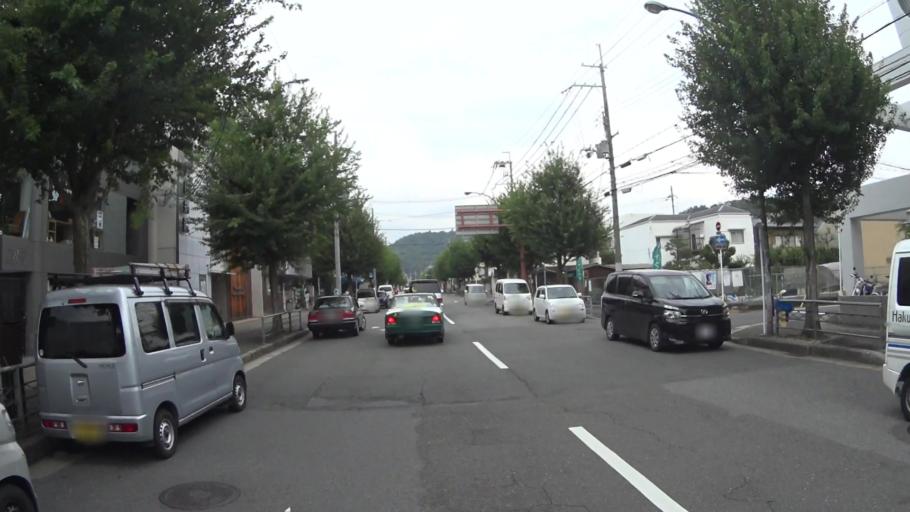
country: JP
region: Kyoto
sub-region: Kyoto-shi
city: Kamigyo-ku
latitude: 35.0521
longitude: 135.7672
